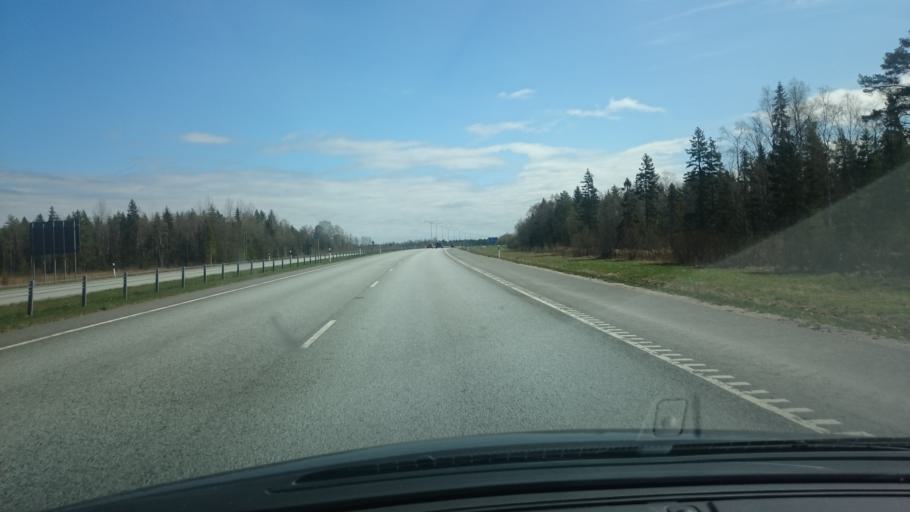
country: EE
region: Laeaene-Virumaa
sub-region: Tapa vald
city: Tapa
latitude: 59.4606
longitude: 25.9861
